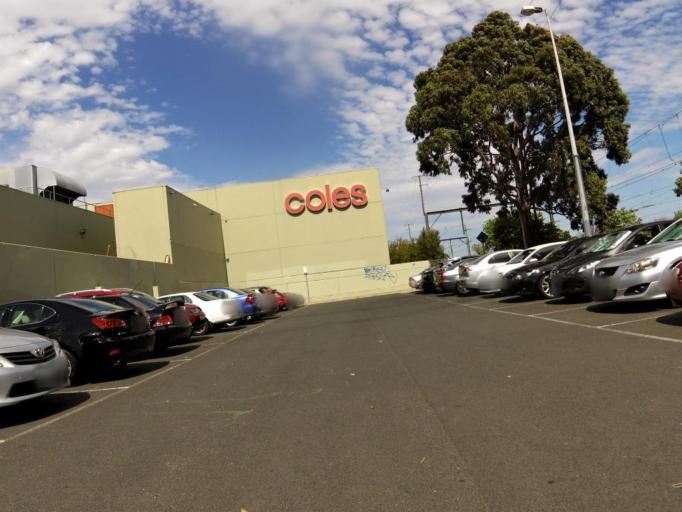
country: AU
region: Victoria
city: Hughesdale
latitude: -37.9008
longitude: 145.0893
